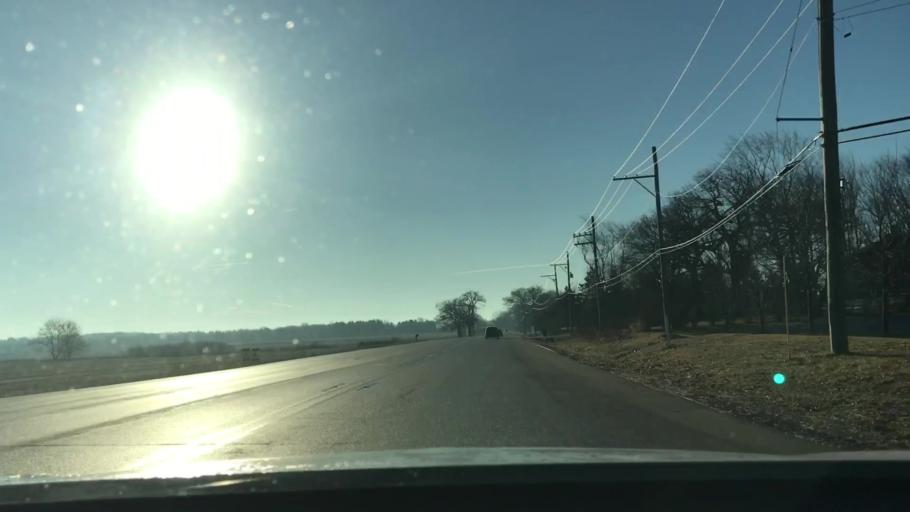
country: US
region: Illinois
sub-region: Kane County
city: Gilberts
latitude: 42.0975
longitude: -88.4022
